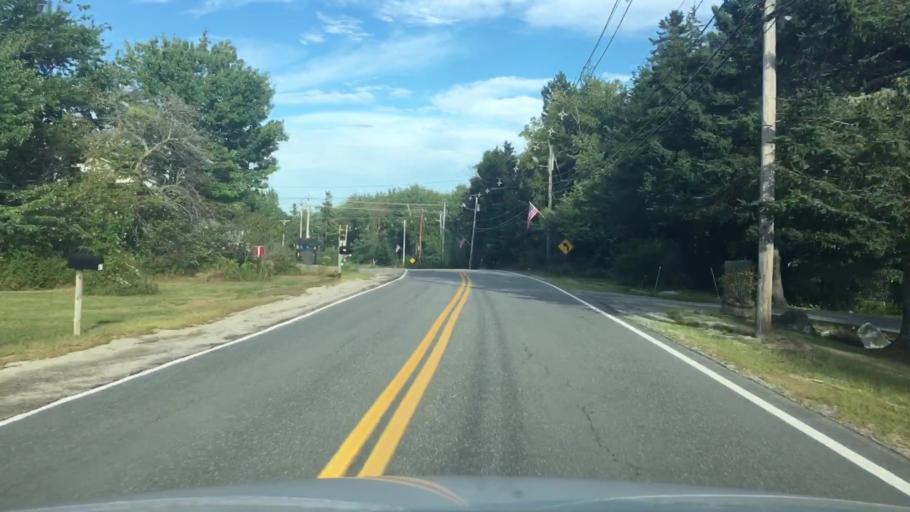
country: US
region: Maine
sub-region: Hancock County
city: Trenton
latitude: 44.4375
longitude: -68.3756
